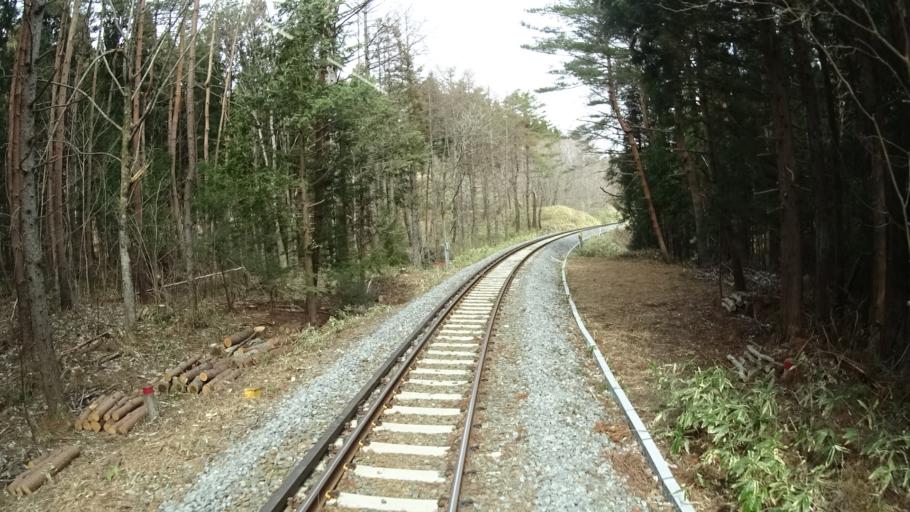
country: JP
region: Iwate
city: Yamada
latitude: 39.5027
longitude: 141.9264
